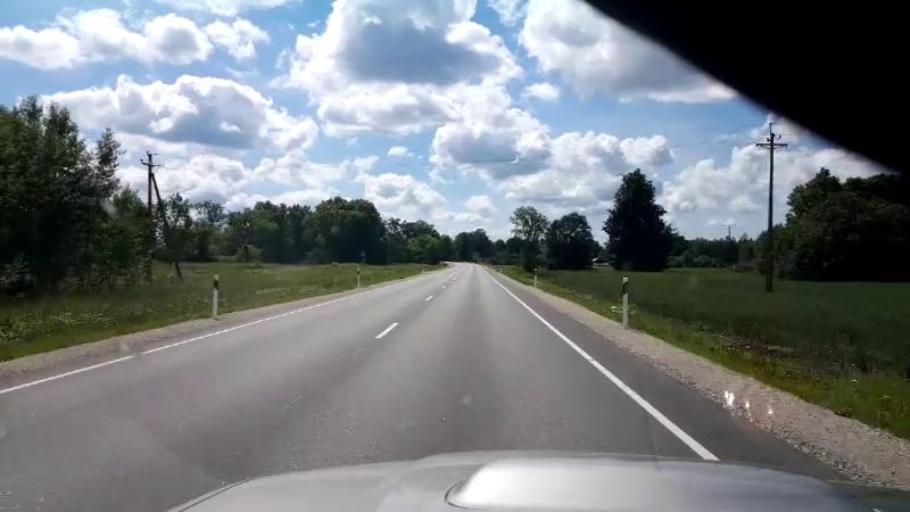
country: EE
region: Jaervamaa
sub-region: Jaerva-Jaani vald
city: Jarva-Jaani
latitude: 59.0747
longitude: 25.6835
